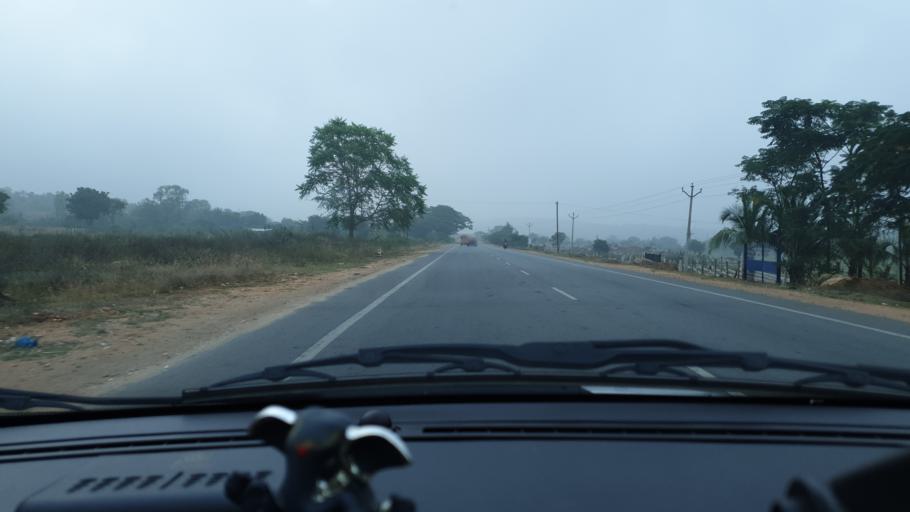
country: IN
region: Telangana
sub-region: Mahbubnagar
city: Farrukhnagar
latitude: 16.9618
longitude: 78.5116
